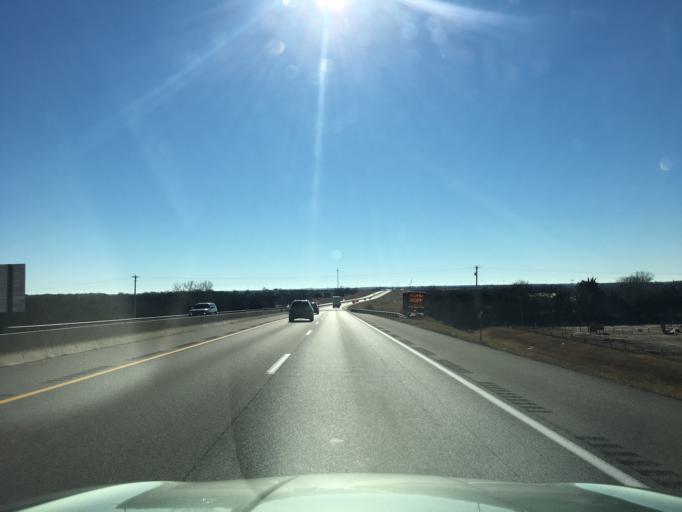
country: US
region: Kansas
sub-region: Sumner County
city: Wellington
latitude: 37.2629
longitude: -97.3396
